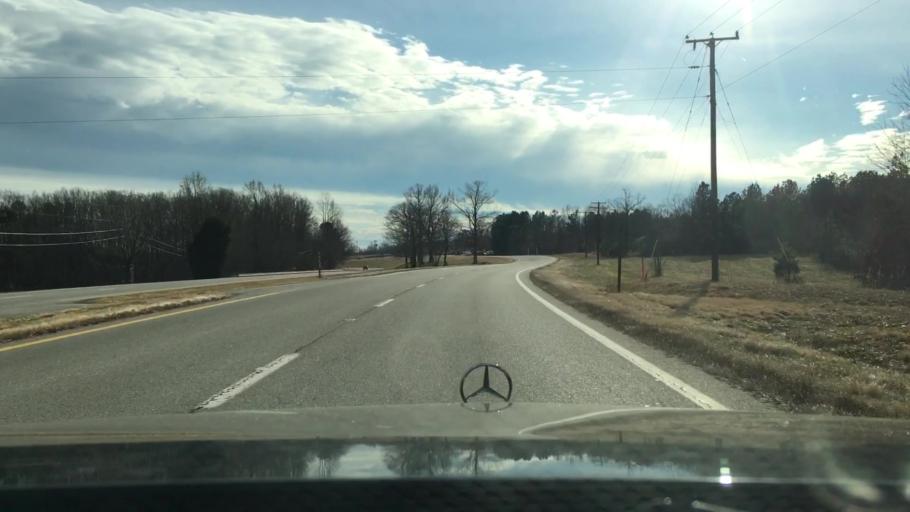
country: US
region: Virginia
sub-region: Pittsylvania County
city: Mount Hermon
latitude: 36.7277
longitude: -79.3840
